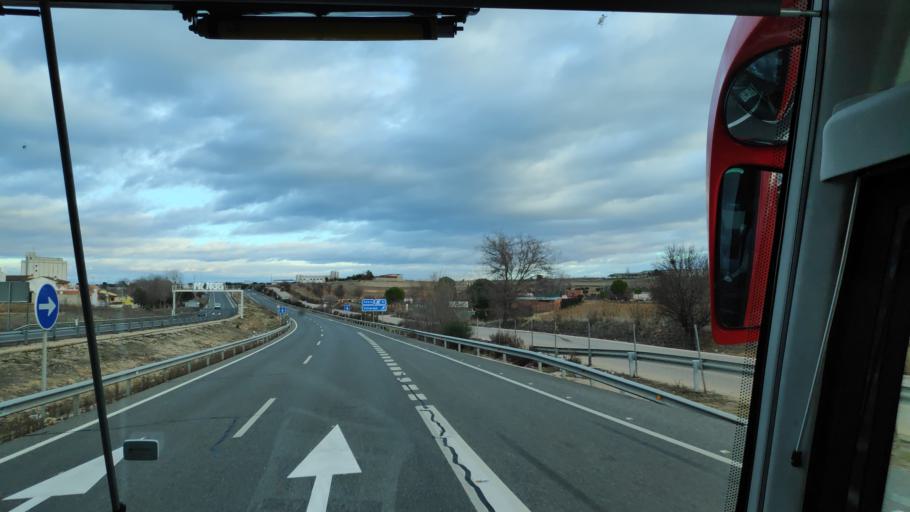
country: ES
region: Madrid
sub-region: Provincia de Madrid
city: Villarejo de Salvanes
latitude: 40.1647
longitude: -3.2799
